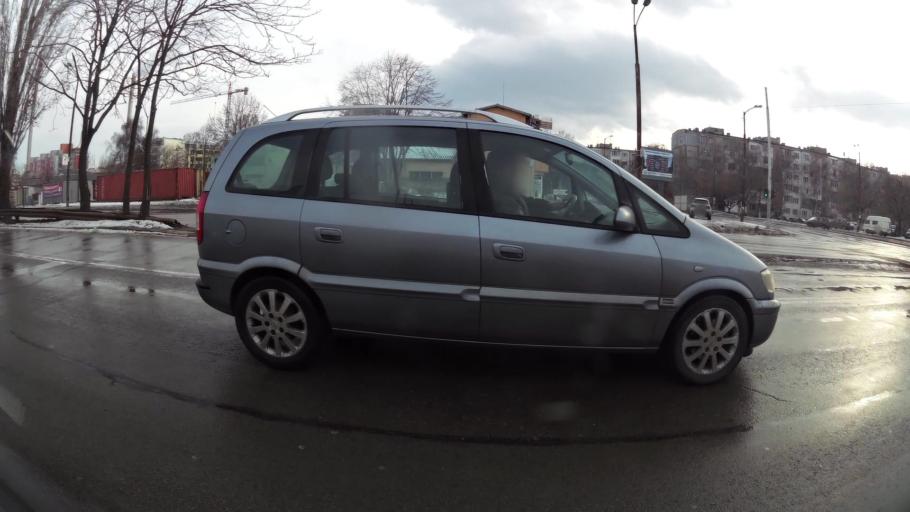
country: BG
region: Sofia-Capital
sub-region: Stolichna Obshtina
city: Sofia
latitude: 42.7115
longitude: 23.3549
